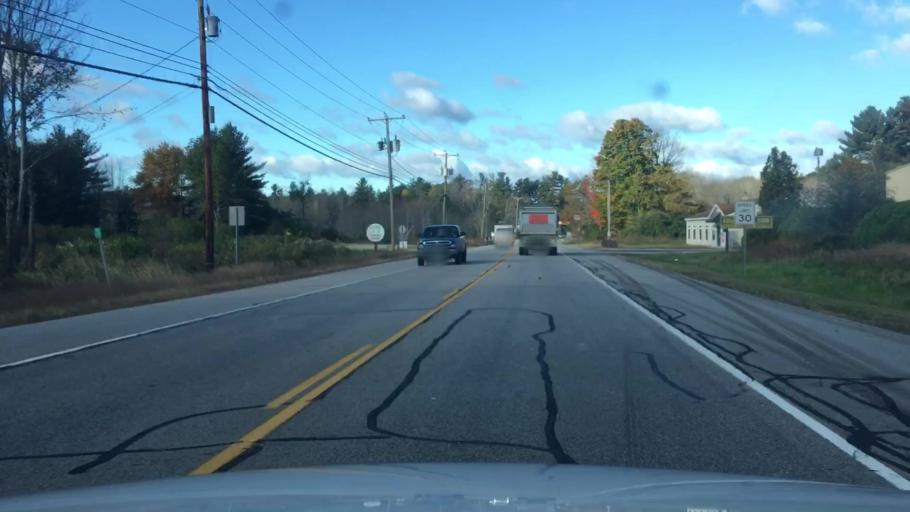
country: US
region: New Hampshire
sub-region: Strafford County
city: Lee
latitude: 43.1488
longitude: -70.9982
